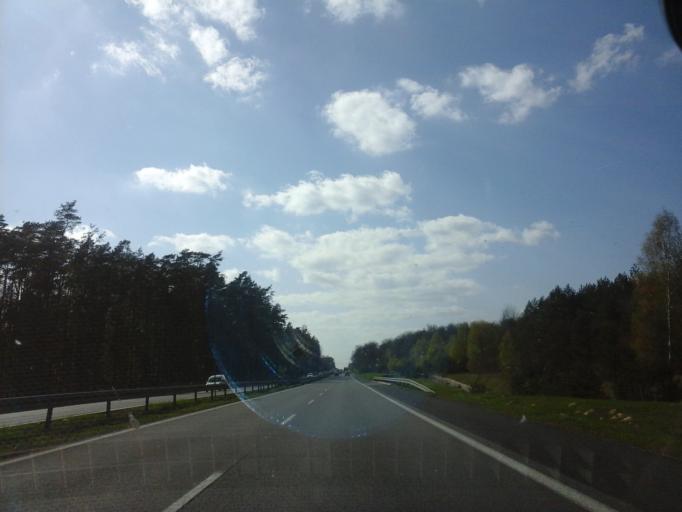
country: PL
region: West Pomeranian Voivodeship
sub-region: Powiat stargardzki
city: Kobylanka
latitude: 53.3520
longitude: 14.8177
